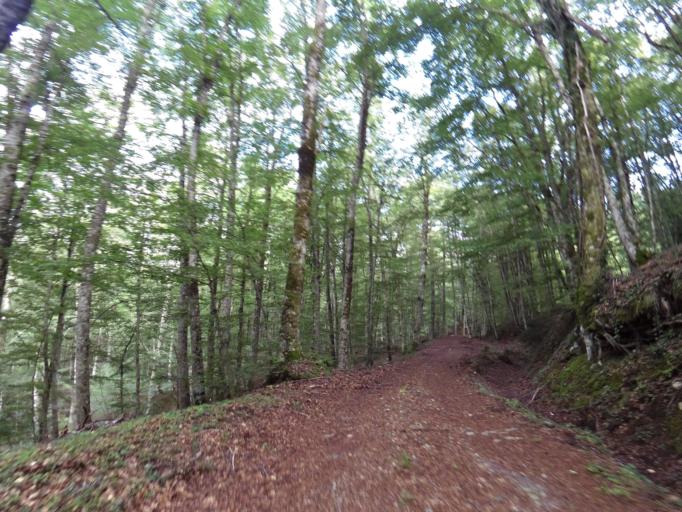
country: IT
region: Calabria
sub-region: Provincia di Vibo-Valentia
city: Nardodipace
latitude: 38.5208
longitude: 16.3814
